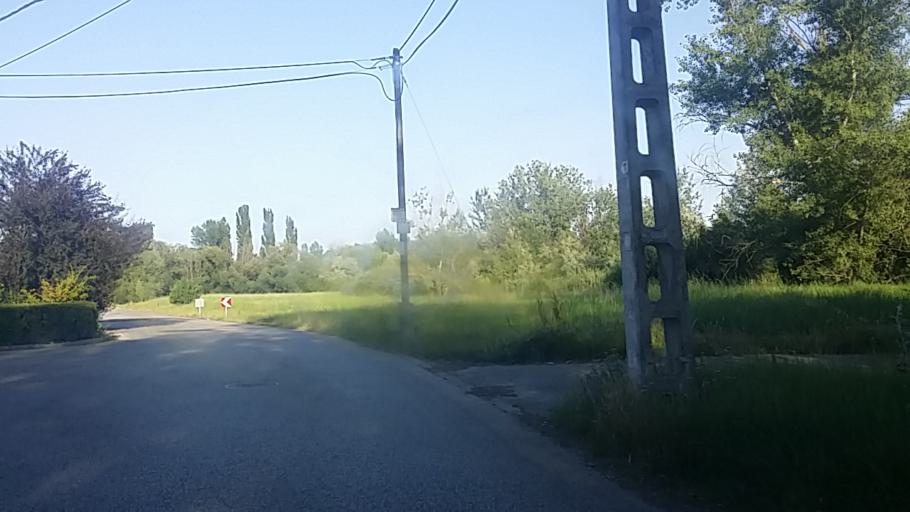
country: HU
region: Pest
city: Urom
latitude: 47.5791
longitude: 19.0377
